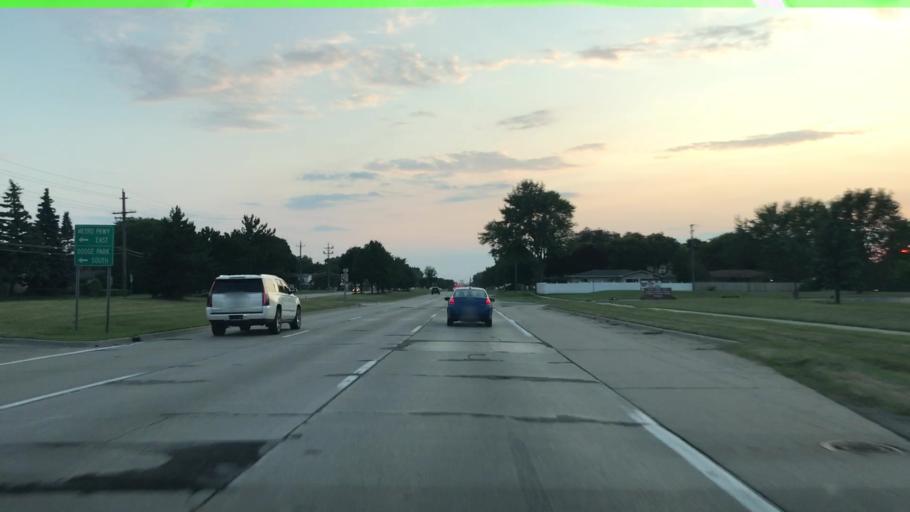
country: US
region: Michigan
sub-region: Macomb County
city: Sterling Heights
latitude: 42.5666
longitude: -83.0123
